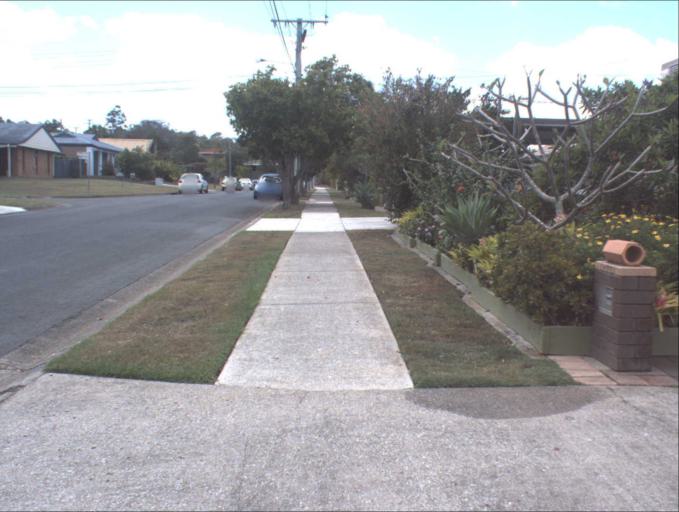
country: AU
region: Queensland
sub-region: Logan
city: Slacks Creek
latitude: -27.6334
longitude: 153.1420
